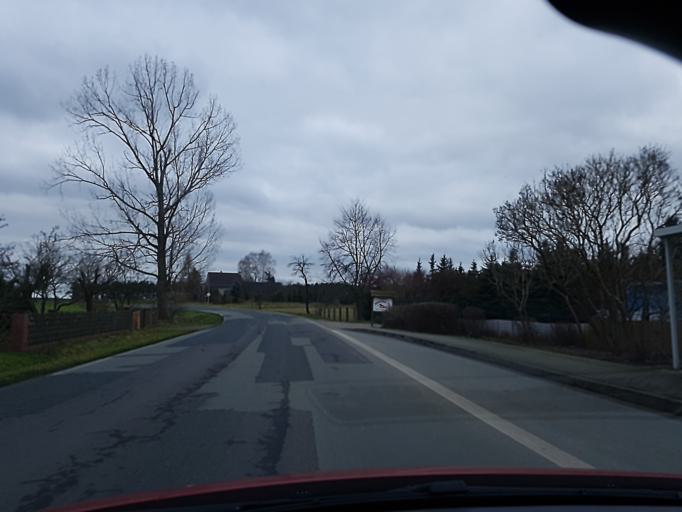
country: DE
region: Brandenburg
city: Trobitz
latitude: 51.5587
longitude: 13.4184
